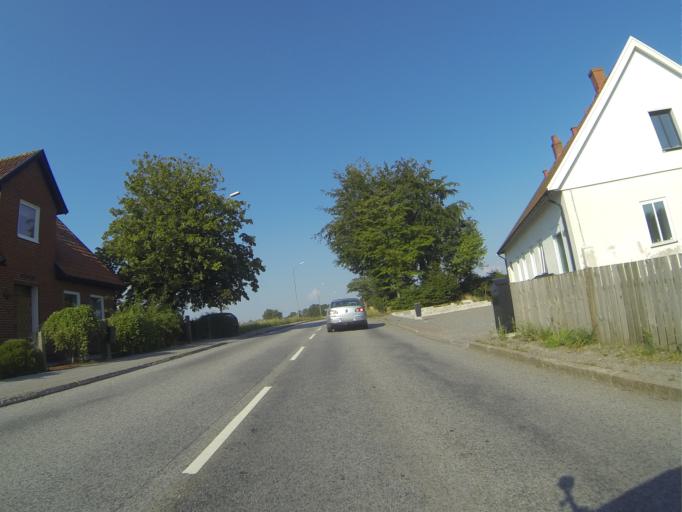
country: SE
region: Skane
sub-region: Svedala Kommun
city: Klagerup
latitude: 55.5806
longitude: 13.1958
